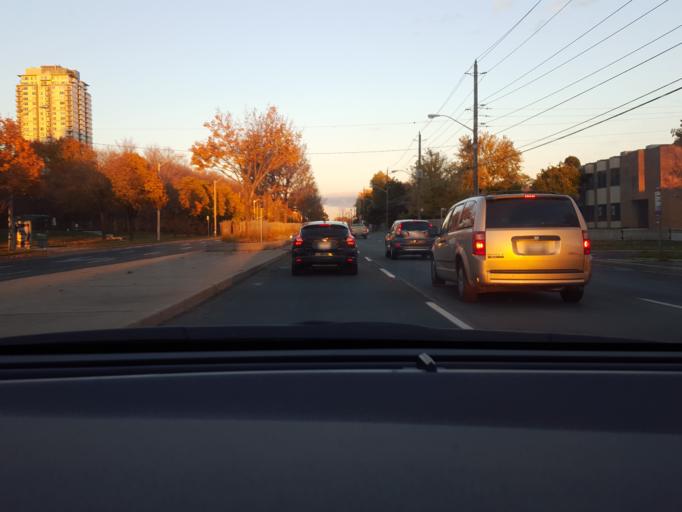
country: CA
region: Ontario
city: Scarborough
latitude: 43.7708
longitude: -79.2582
